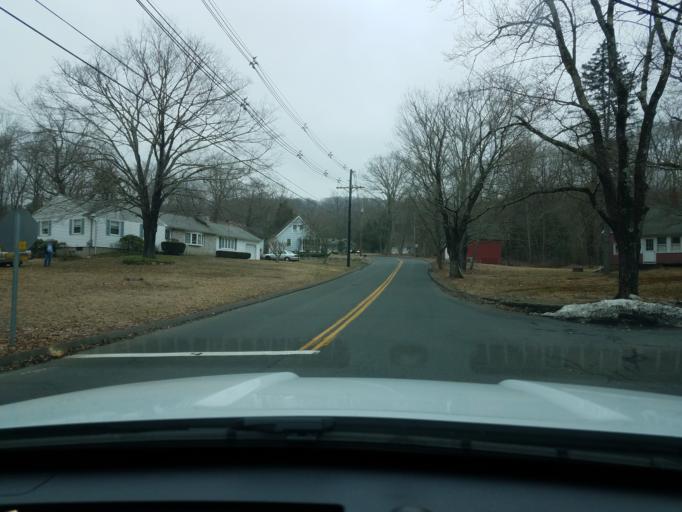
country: US
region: Connecticut
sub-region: New Haven County
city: Naugatuck
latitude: 41.4387
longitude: -73.0390
